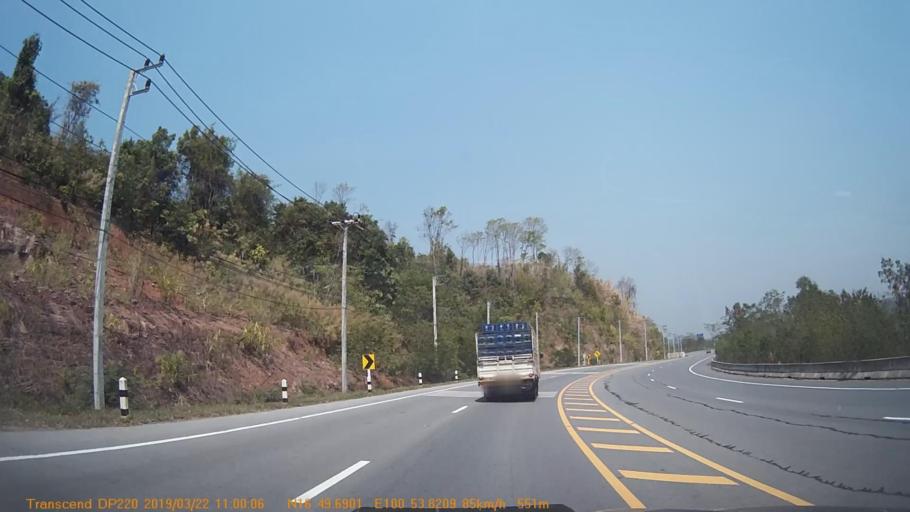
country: TH
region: Phetchabun
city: Khao Kho
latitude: 16.8282
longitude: 100.8965
